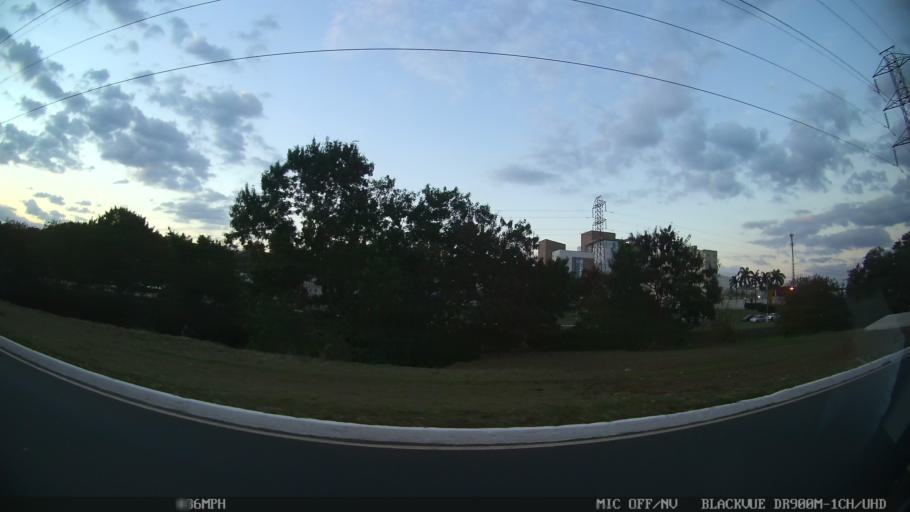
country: BR
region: Sao Paulo
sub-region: Ribeirao Preto
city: Ribeirao Preto
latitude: -21.2107
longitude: -47.7808
